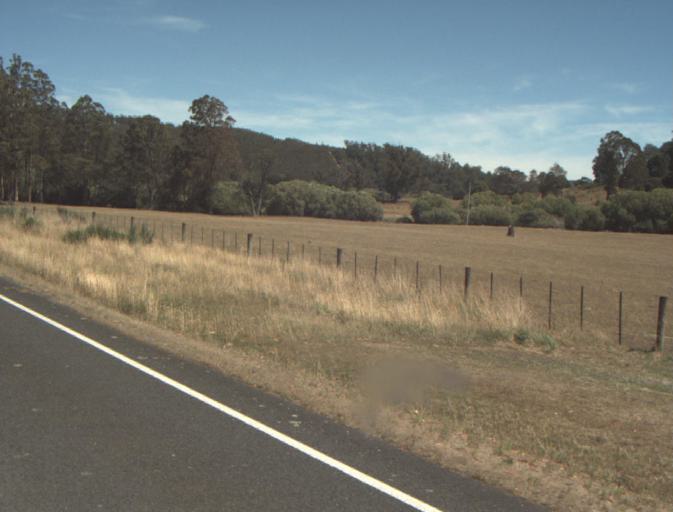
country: AU
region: Tasmania
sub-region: Dorset
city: Scottsdale
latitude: -41.3025
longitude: 147.3818
